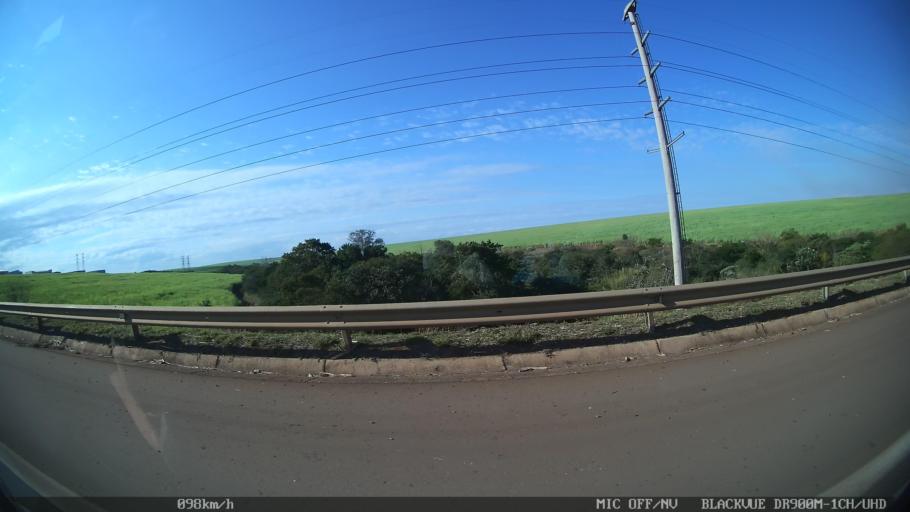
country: BR
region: Sao Paulo
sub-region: Piracicaba
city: Piracicaba
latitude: -22.6752
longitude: -47.5989
